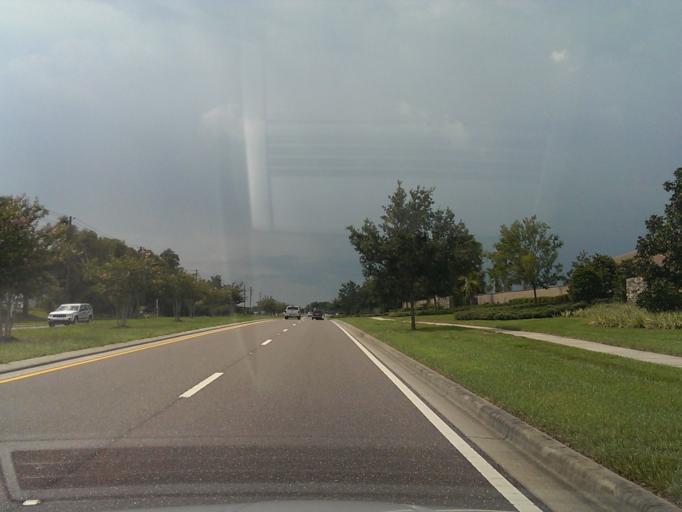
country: US
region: Florida
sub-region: Orange County
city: Lake Butler
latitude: 28.4732
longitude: -81.5674
